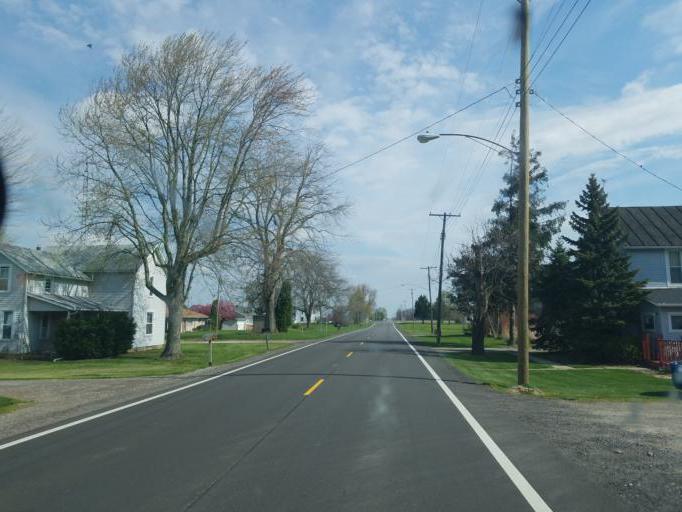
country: US
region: Ohio
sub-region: Crawford County
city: Bucyrus
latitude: 40.6917
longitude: -83.0077
